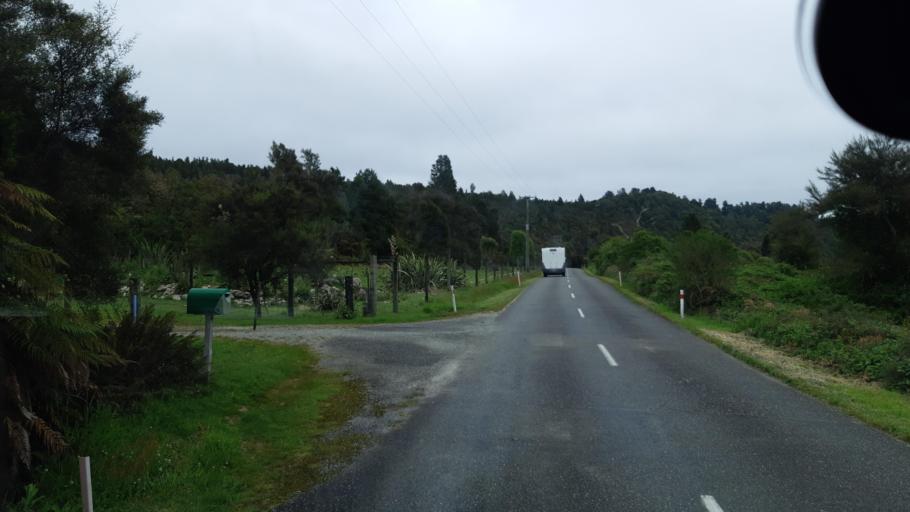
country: NZ
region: West Coast
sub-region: Grey District
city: Greymouth
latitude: -42.6355
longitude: 171.2773
